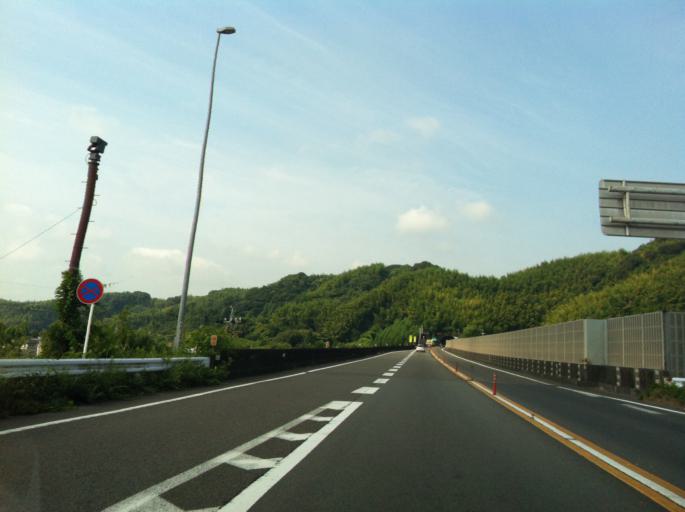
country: JP
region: Shizuoka
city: Fujieda
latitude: 34.8966
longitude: 138.2759
